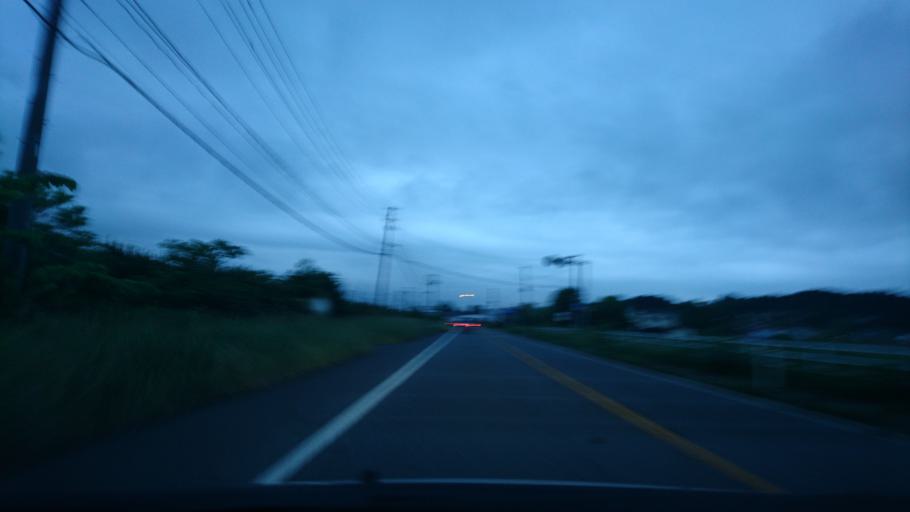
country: JP
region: Iwate
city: Ichinoseki
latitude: 38.8187
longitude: 141.0772
